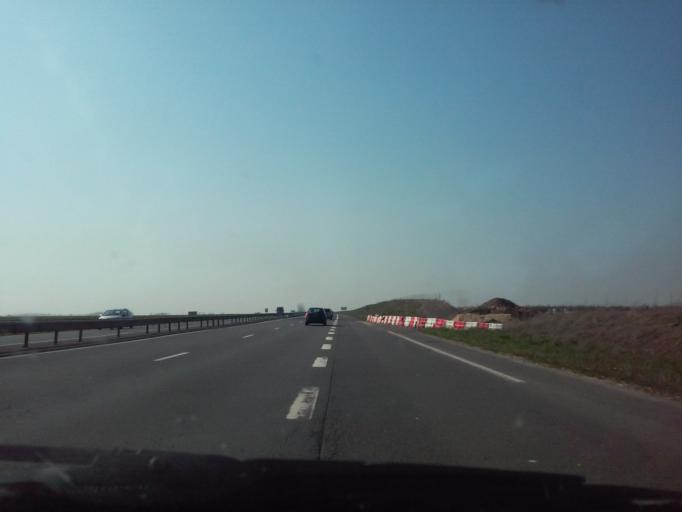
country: FR
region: Lower Normandy
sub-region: Departement du Calvados
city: Cheux
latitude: 49.2219
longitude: -0.5463
